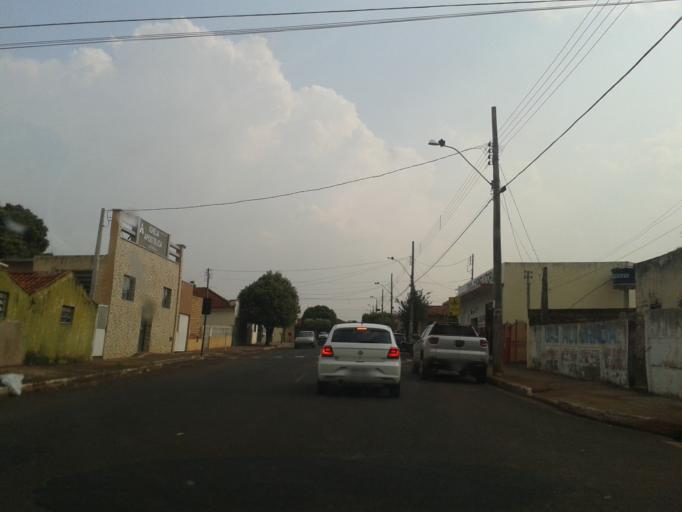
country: BR
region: Minas Gerais
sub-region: Ituiutaba
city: Ituiutaba
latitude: -18.9736
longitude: -49.4738
